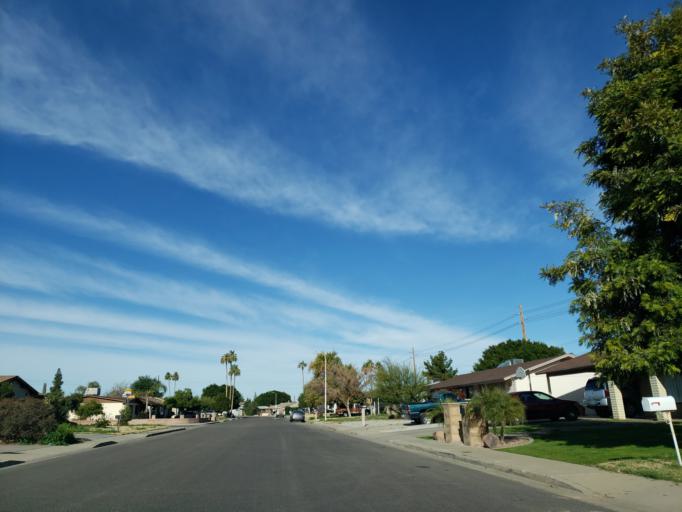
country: US
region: Arizona
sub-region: Maricopa County
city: Glendale
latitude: 33.5797
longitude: -112.1490
